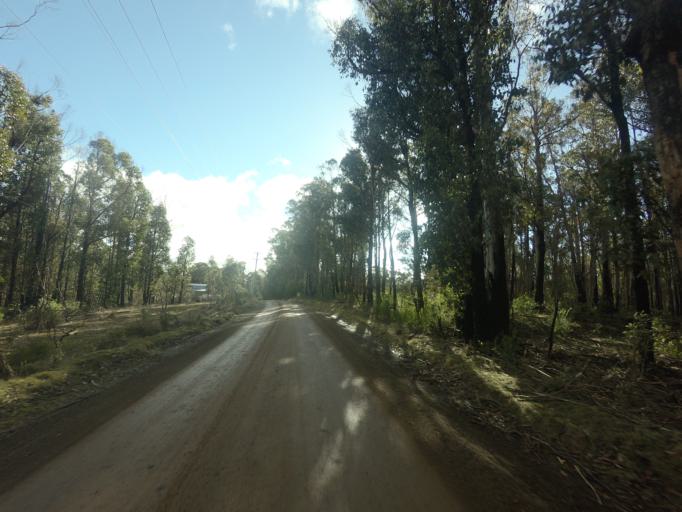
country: AU
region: Tasmania
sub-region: Derwent Valley
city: New Norfolk
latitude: -42.8383
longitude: 147.1346
